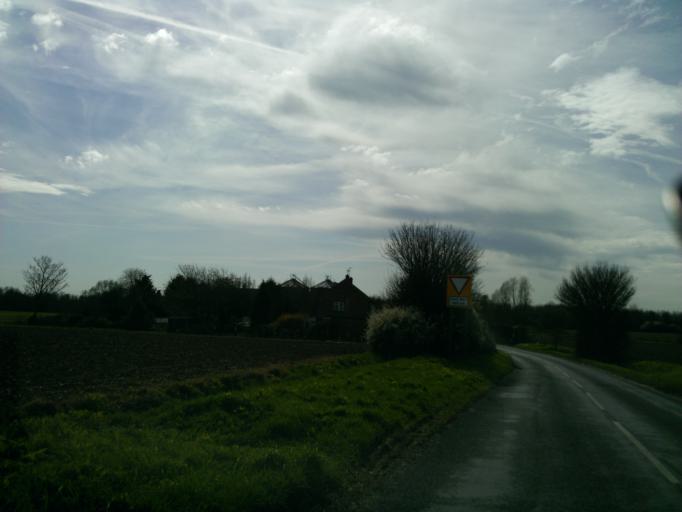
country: GB
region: England
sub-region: Essex
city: Witham
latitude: 51.8428
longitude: 0.6479
